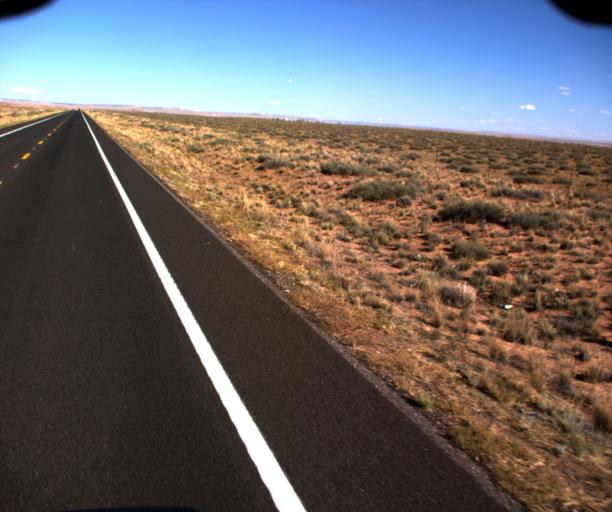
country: US
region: Arizona
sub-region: Coconino County
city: Tuba City
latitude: 36.1609
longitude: -111.1055
